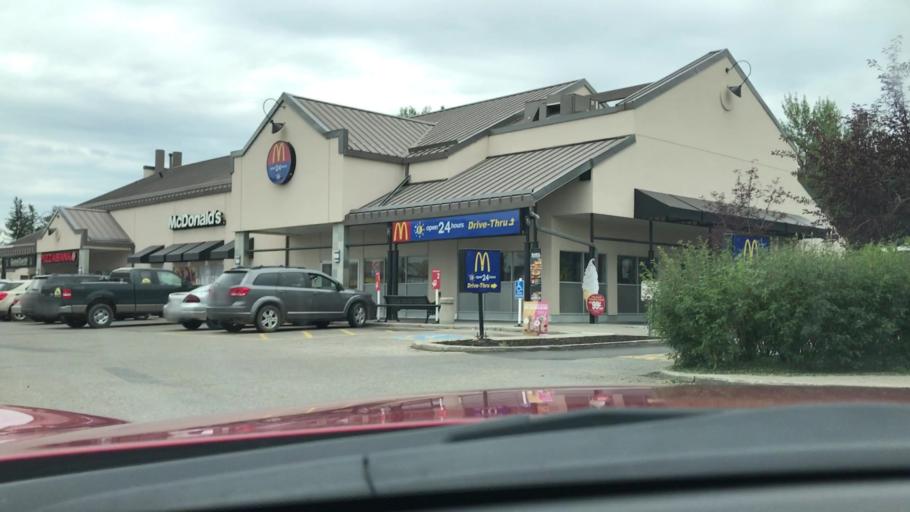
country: CA
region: Alberta
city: Calgary
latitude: 50.9739
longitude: -114.0989
